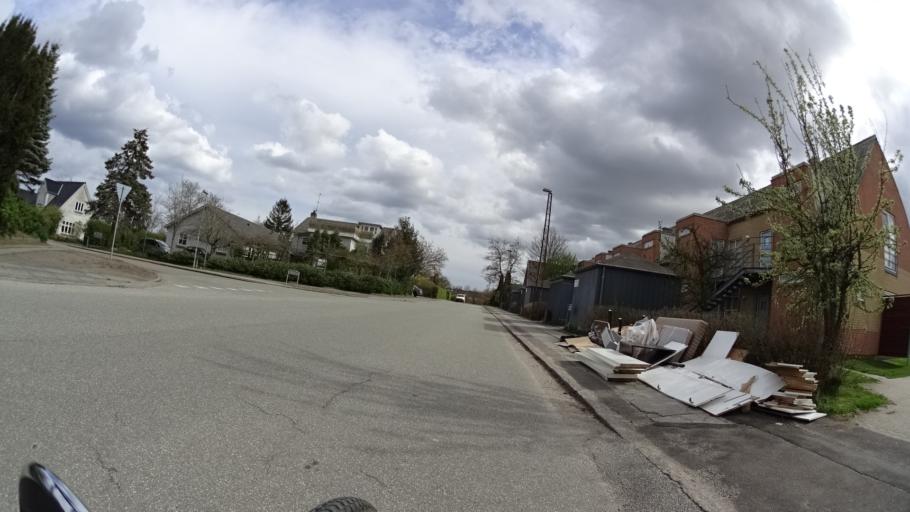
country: DK
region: Central Jutland
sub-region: Arhus Kommune
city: Stavtrup
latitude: 56.1312
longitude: 10.1494
